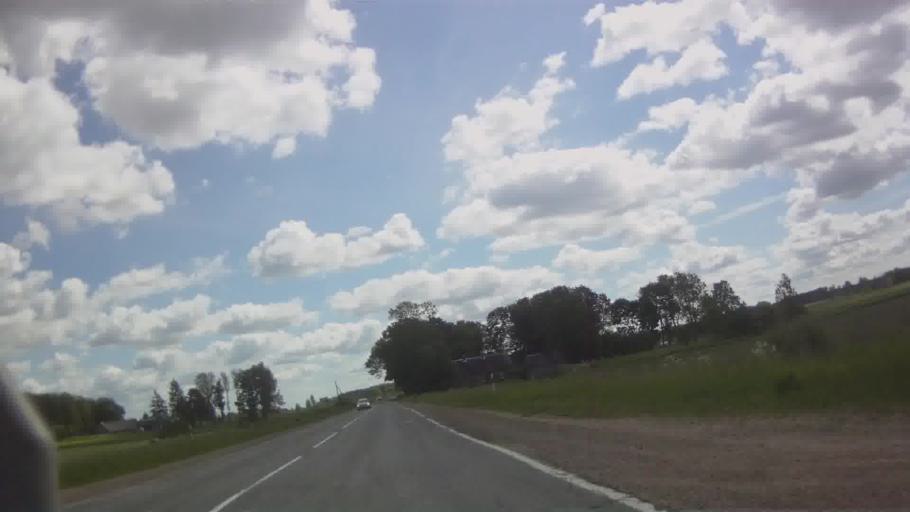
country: LV
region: Vilanu
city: Vilani
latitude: 56.5970
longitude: 26.8737
